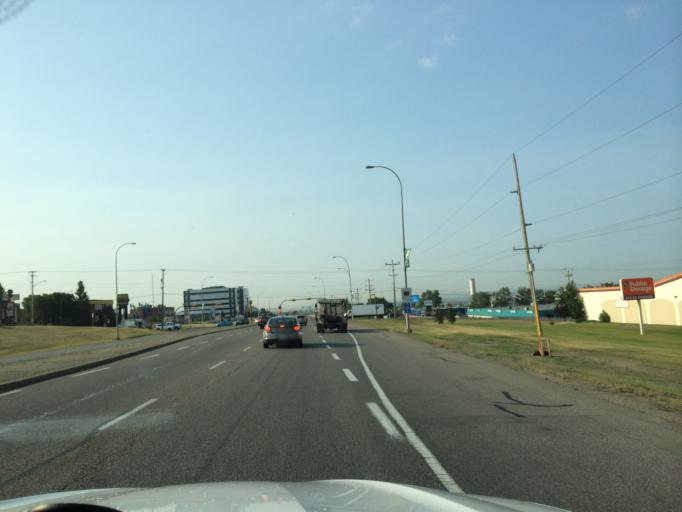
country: CA
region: Alberta
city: Calgary
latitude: 51.0538
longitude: -114.0018
